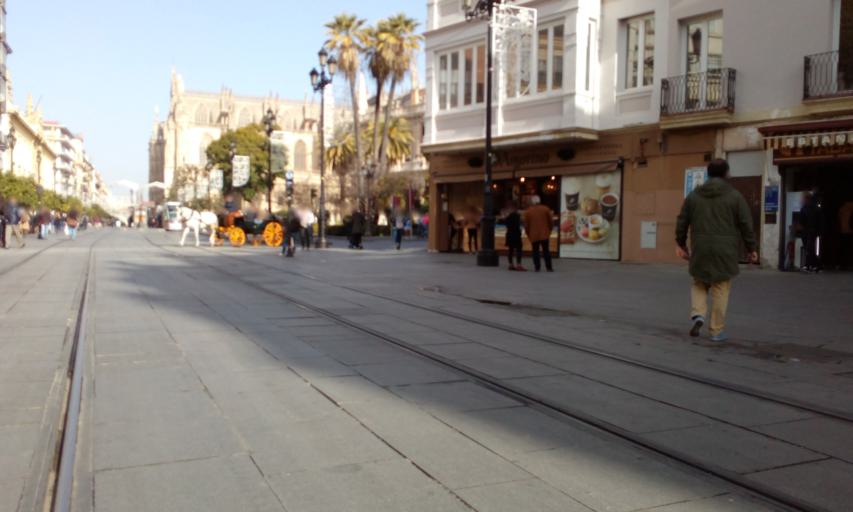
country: ES
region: Andalusia
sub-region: Provincia de Sevilla
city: Sevilla
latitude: 37.3837
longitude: -5.9936
